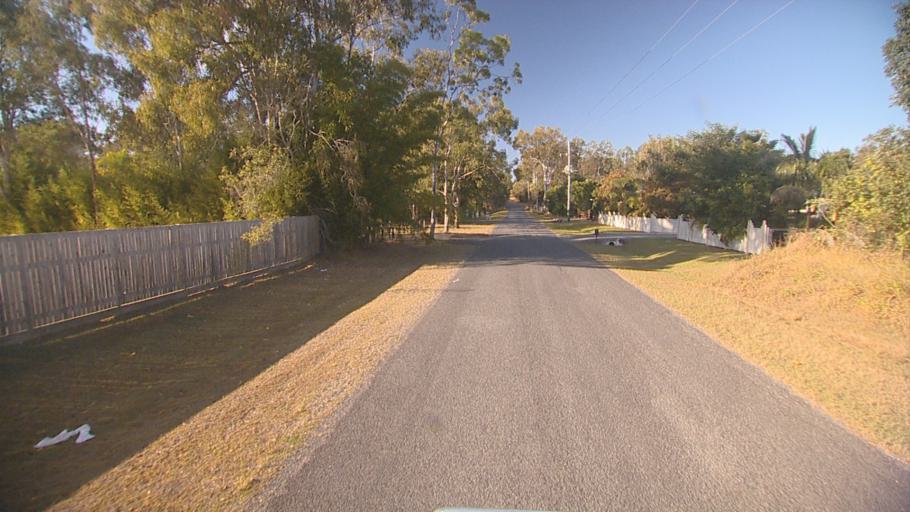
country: AU
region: Queensland
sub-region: Logan
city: Park Ridge South
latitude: -27.7201
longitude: 152.9716
